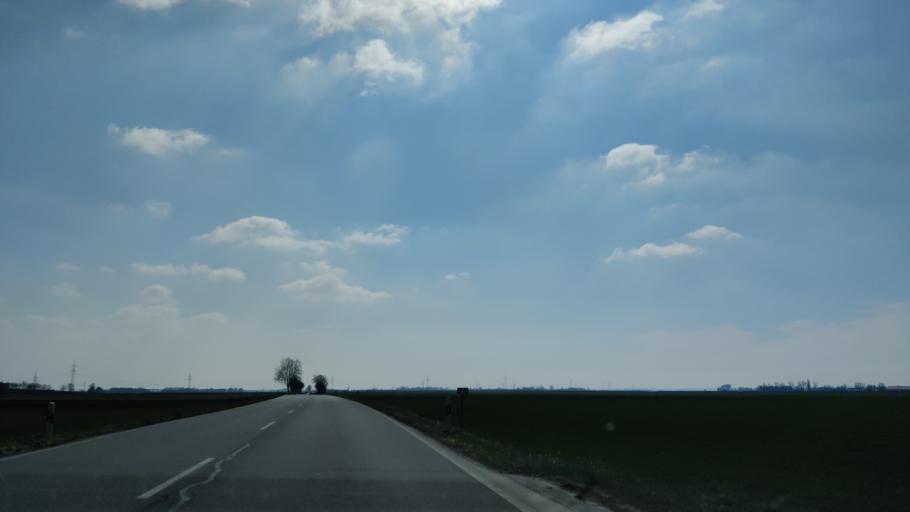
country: DE
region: Bavaria
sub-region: Lower Bavaria
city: Irlbach
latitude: 48.8205
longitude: 12.7481
